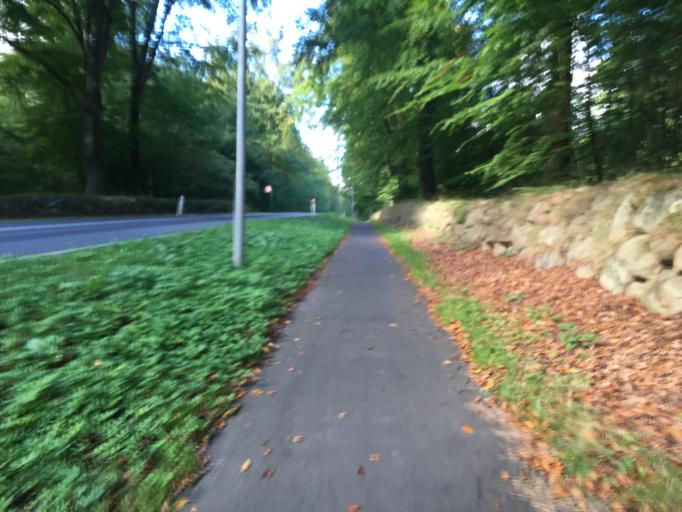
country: DK
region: Capital Region
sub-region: Fureso Kommune
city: Vaerlose
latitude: 55.7684
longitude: 12.3947
